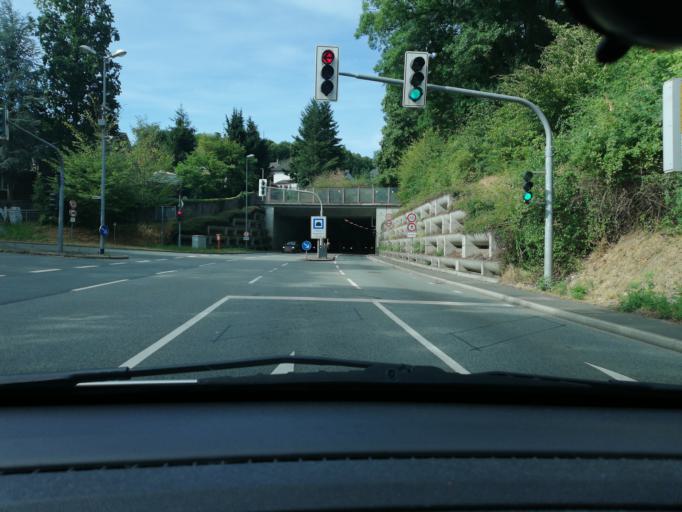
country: DE
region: North Rhine-Westphalia
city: Gevelsberg
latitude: 51.3169
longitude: 7.3387
